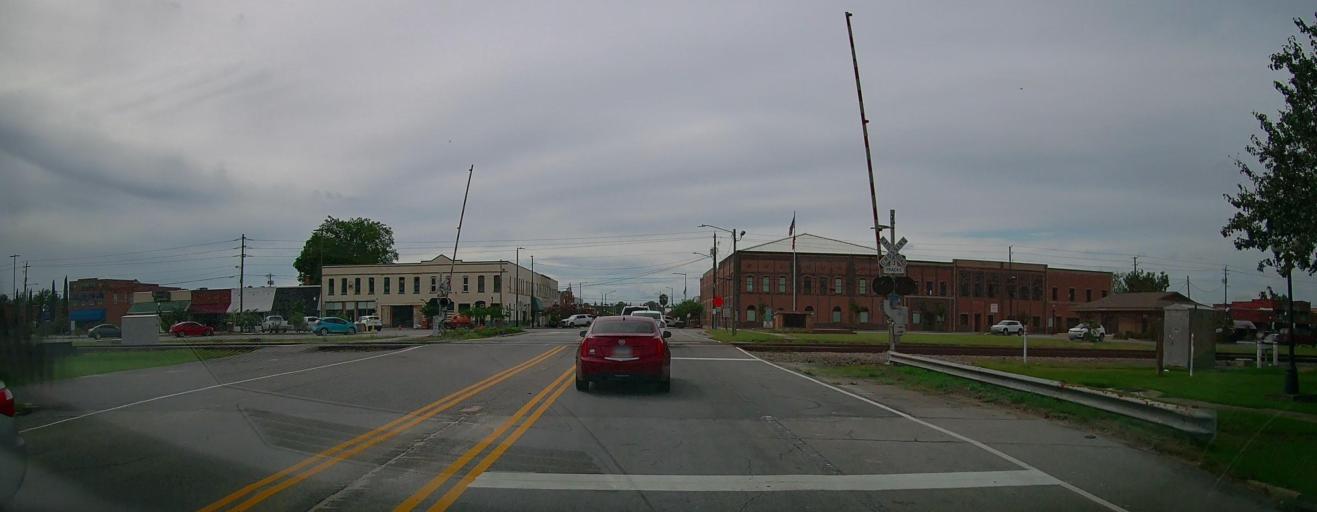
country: US
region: Georgia
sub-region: Wayne County
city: Jesup
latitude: 31.6047
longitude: -81.8823
